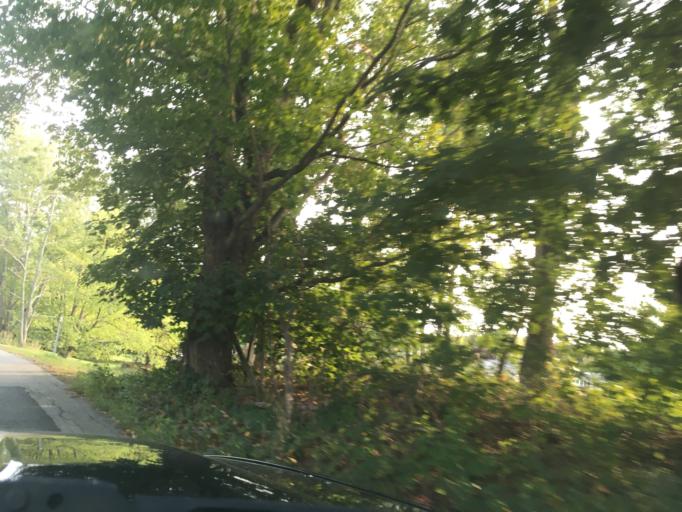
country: US
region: New Hampshire
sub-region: Rockingham County
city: Stratham Station
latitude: 42.9946
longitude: -70.8869
